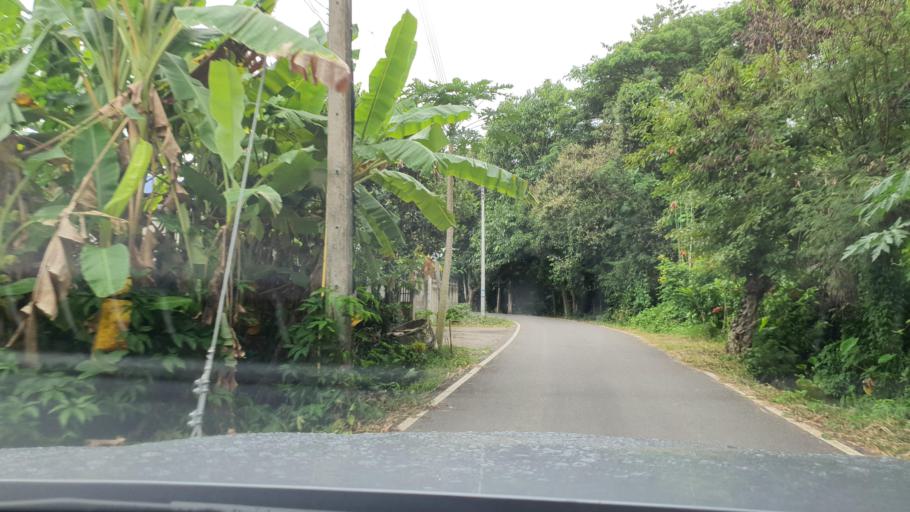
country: TH
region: Chiang Mai
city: Hang Dong
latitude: 18.6649
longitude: 98.9051
